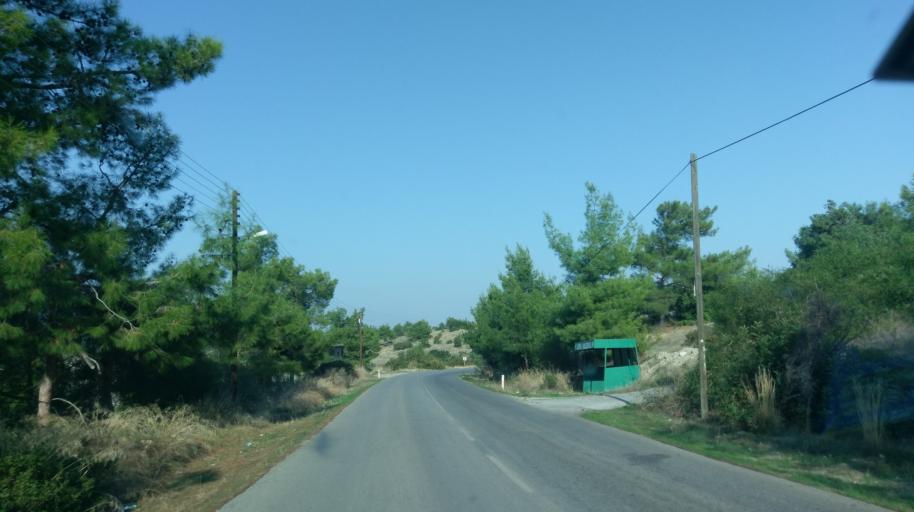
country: CY
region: Lefkosia
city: Kato Pyrgos
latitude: 35.1584
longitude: 32.7654
